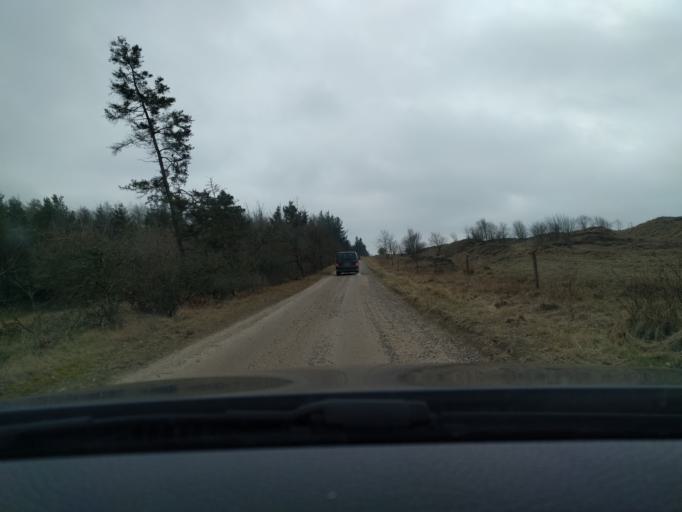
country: DK
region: Central Jutland
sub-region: Skive Kommune
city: Skive
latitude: 56.5151
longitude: 8.9518
